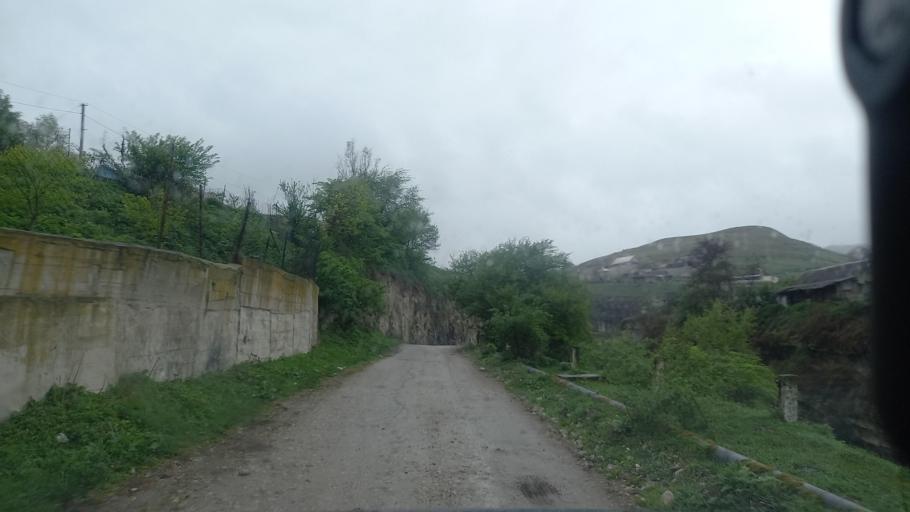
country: RU
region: Kabardino-Balkariya
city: Gundelen
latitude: 43.5968
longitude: 43.1514
